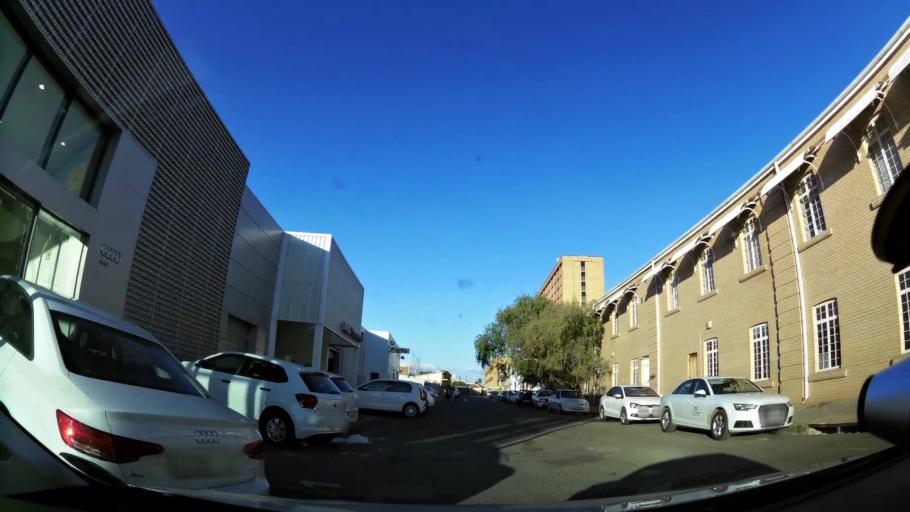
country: ZA
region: Northern Cape
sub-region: Frances Baard District Municipality
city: Kimberley
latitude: -28.7365
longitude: 24.7637
